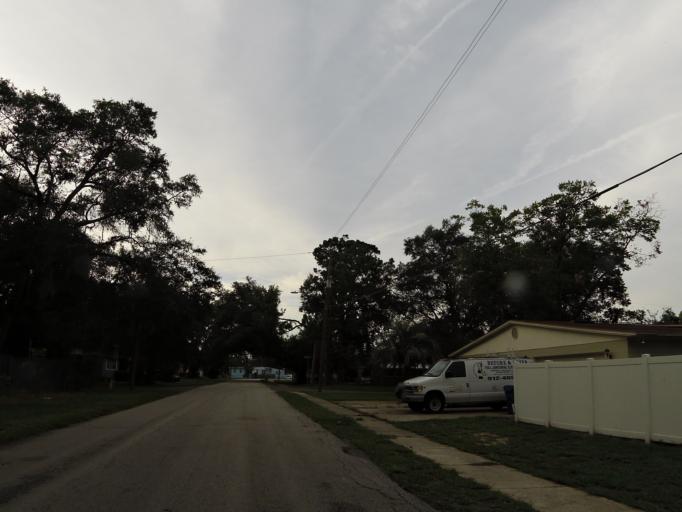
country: US
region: Florida
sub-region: Duval County
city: Jacksonville
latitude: 30.3921
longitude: -81.6976
